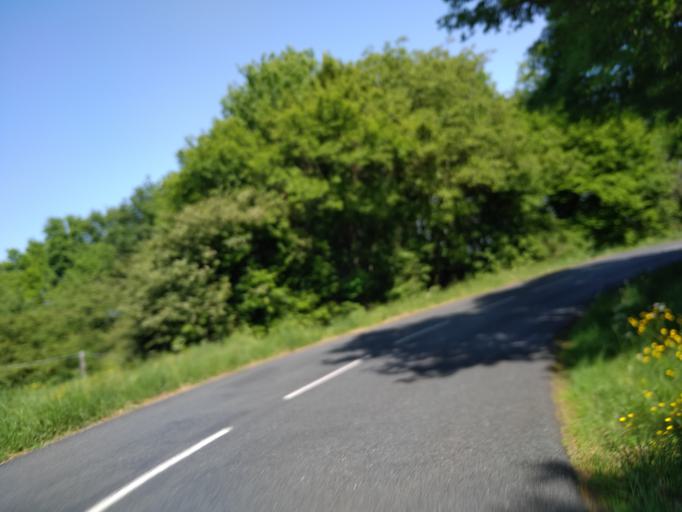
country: FR
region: Rhone-Alpes
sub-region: Departement du Rhone
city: Limonest
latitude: 45.8333
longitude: 4.8036
